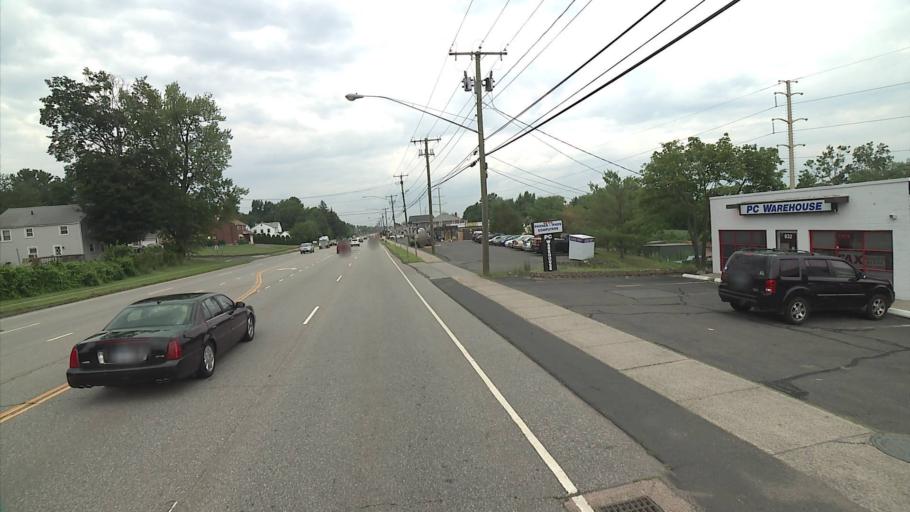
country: US
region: Connecticut
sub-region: Hartford County
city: Wethersfield
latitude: 41.7009
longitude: -72.6594
